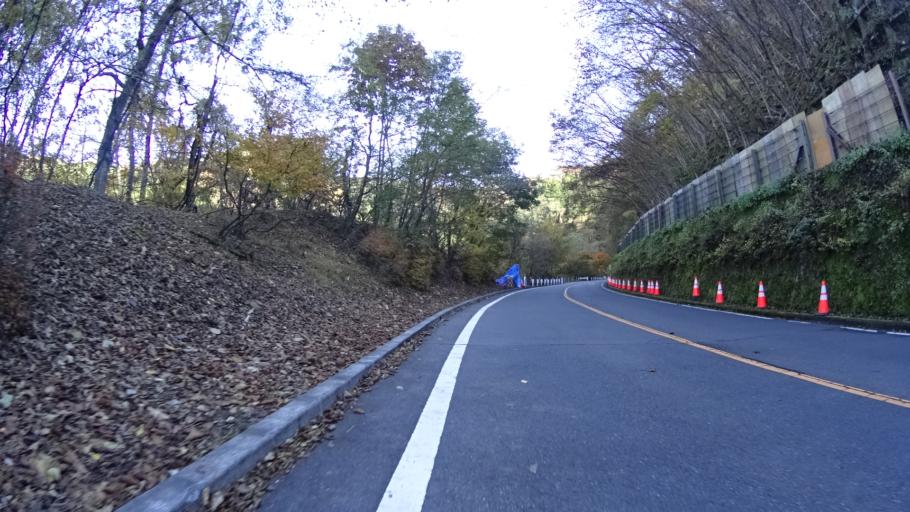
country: JP
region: Yamanashi
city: Uenohara
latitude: 35.7557
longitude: 139.0308
